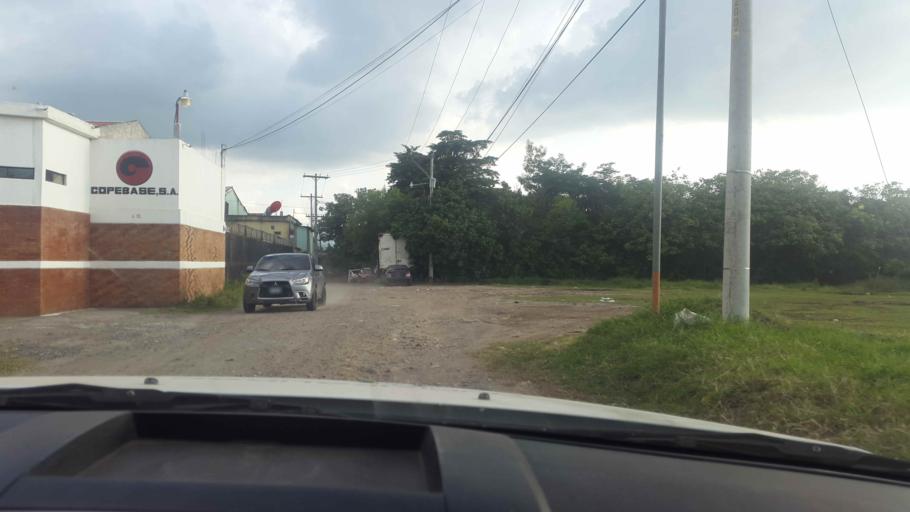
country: GT
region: Guatemala
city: Petapa
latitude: 14.5108
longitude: -90.5447
